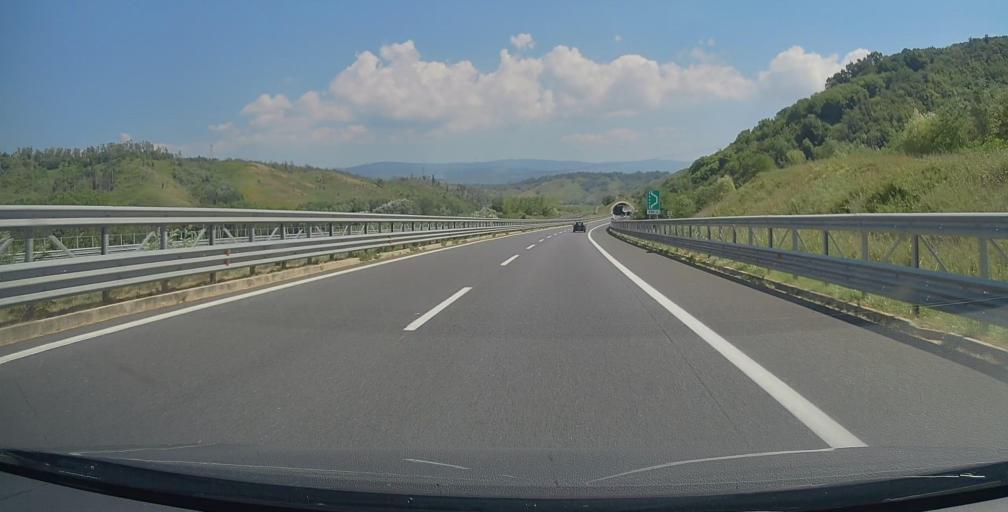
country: IT
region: Calabria
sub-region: Provincia di Vibo-Valentia
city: Filogaso
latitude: 38.6676
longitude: 16.1845
